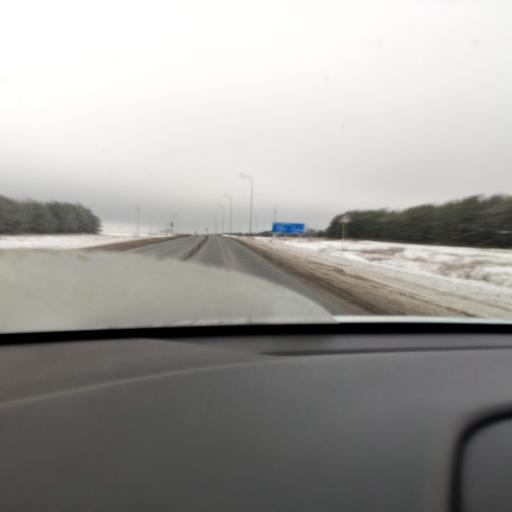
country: RU
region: Tatarstan
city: Verkhniy Uslon
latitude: 55.7098
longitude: 48.8952
